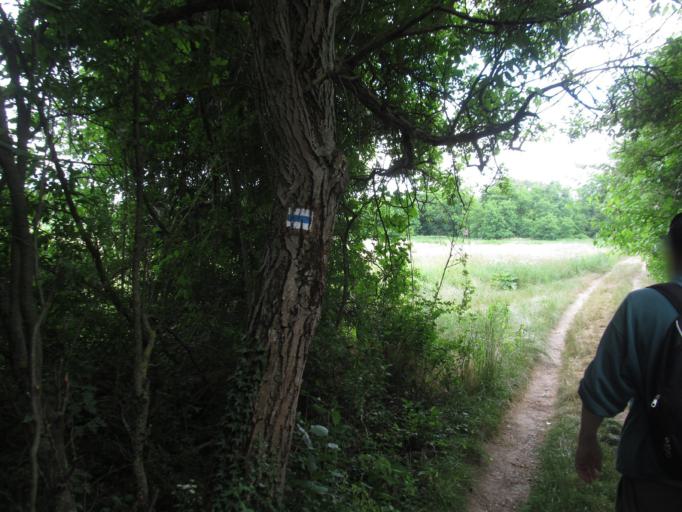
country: HU
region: Veszprem
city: Revfueloep
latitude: 46.8892
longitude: 17.5578
